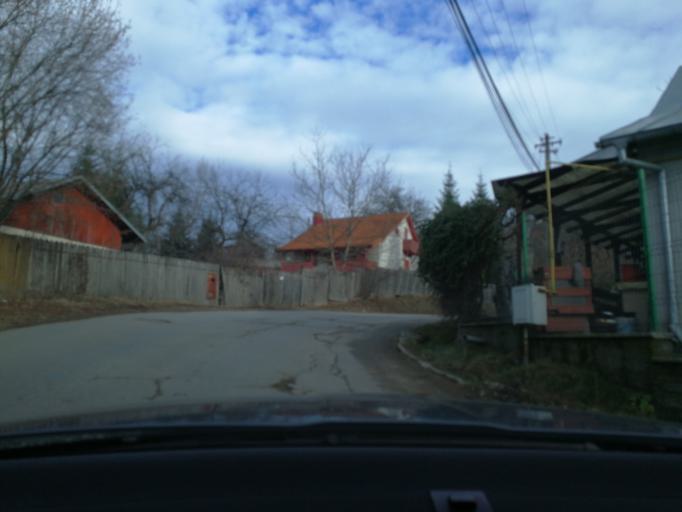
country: RO
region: Prahova
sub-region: Oras Breaza
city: Valea Tarsei
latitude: 45.1791
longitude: 25.6480
